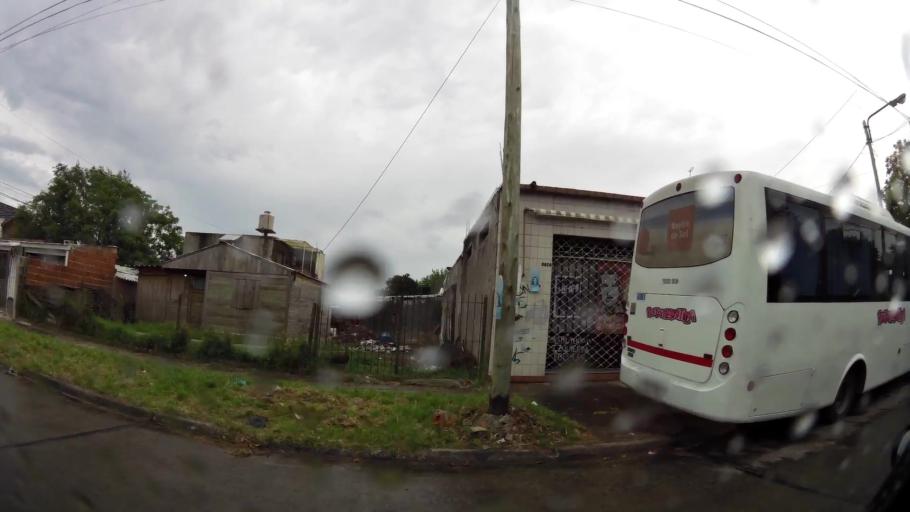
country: AR
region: Buenos Aires
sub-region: Partido de Quilmes
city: Quilmes
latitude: -34.7643
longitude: -58.2248
